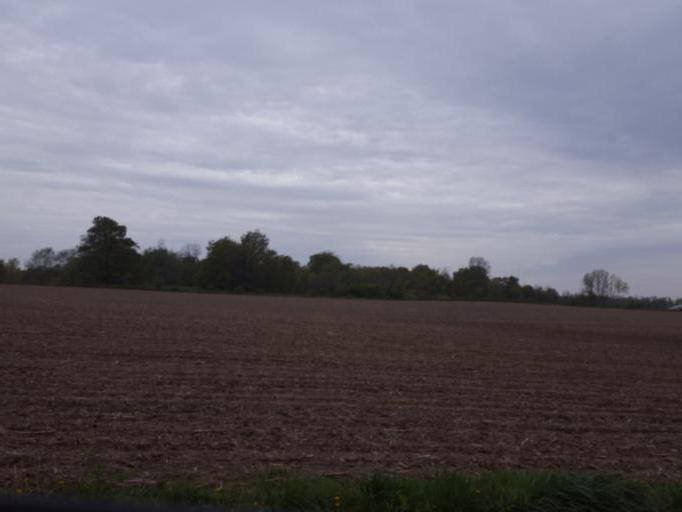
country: US
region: Ohio
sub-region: Richland County
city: Lexington
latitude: 40.6740
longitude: -82.6264
